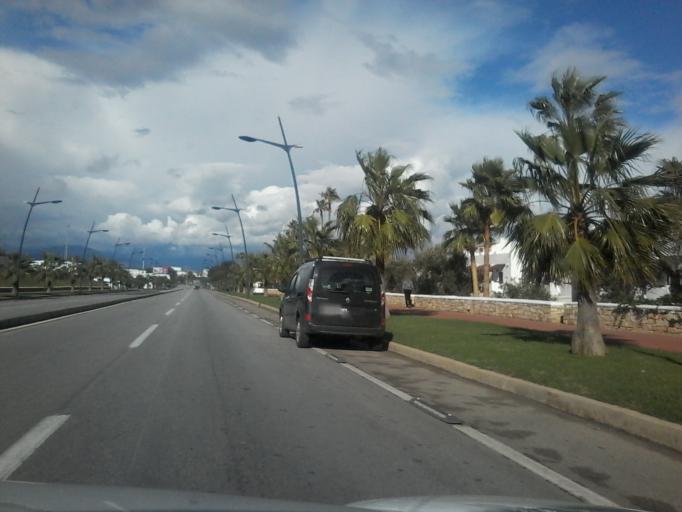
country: MA
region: Tanger-Tetouan
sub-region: Tetouan
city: Martil
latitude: 35.7292
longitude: -5.3406
